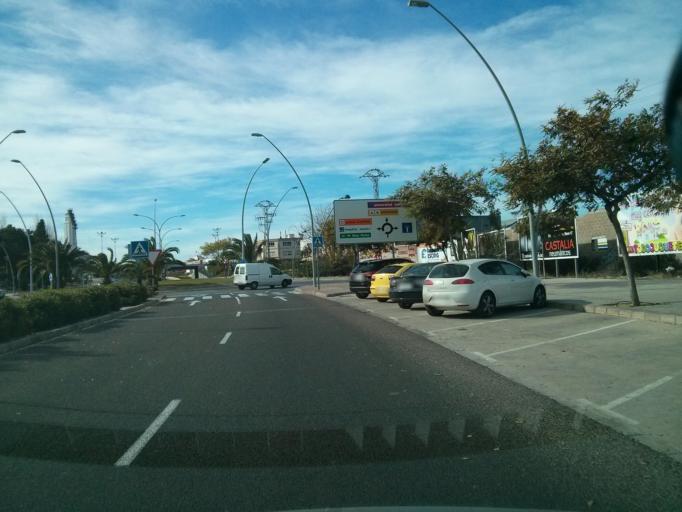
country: ES
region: Valencia
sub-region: Provincia de Castello
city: Castello de la Plana
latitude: 39.9989
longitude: -0.0366
